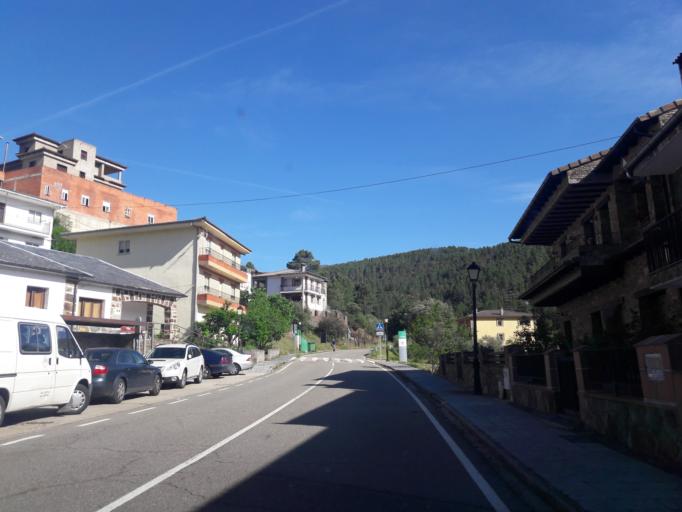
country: ES
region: Castille and Leon
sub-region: Provincia de Salamanca
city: Herguijuela de la Sierra
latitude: 40.4048
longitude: -6.0848
